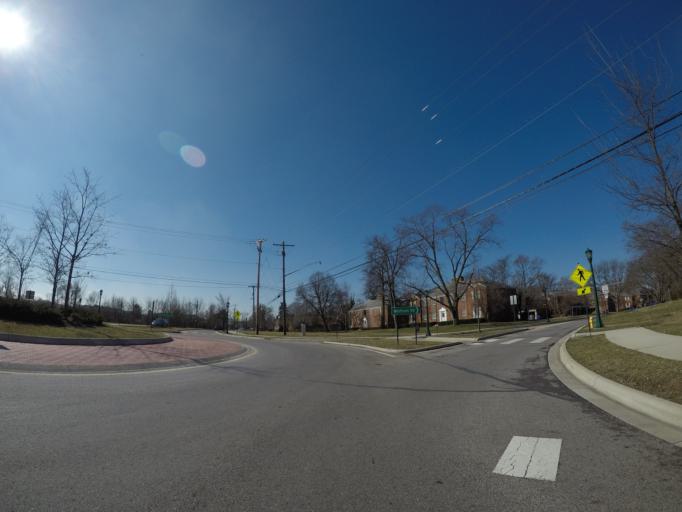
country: US
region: Ohio
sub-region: Franklin County
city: Upper Arlington
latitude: 39.9990
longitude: -83.0482
